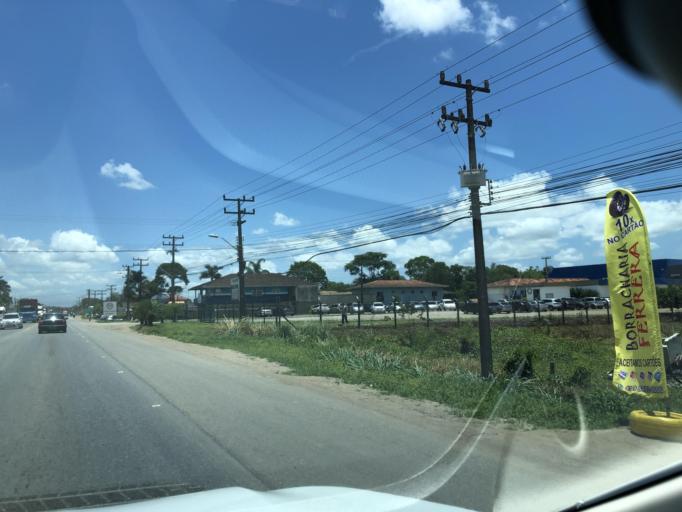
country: BR
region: Santa Catarina
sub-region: Joinville
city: Joinville
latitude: -26.4076
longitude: -48.7490
